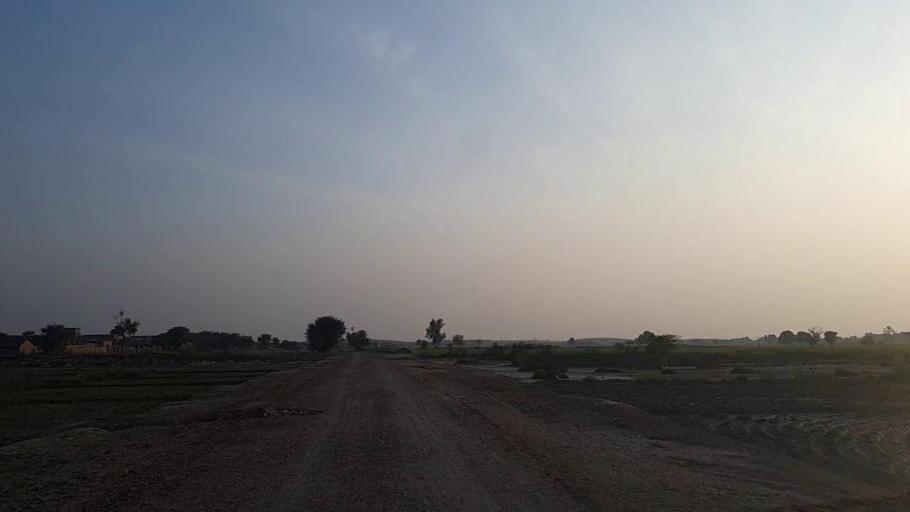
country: PK
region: Sindh
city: Jam Sahib
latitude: 26.4106
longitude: 68.6056
